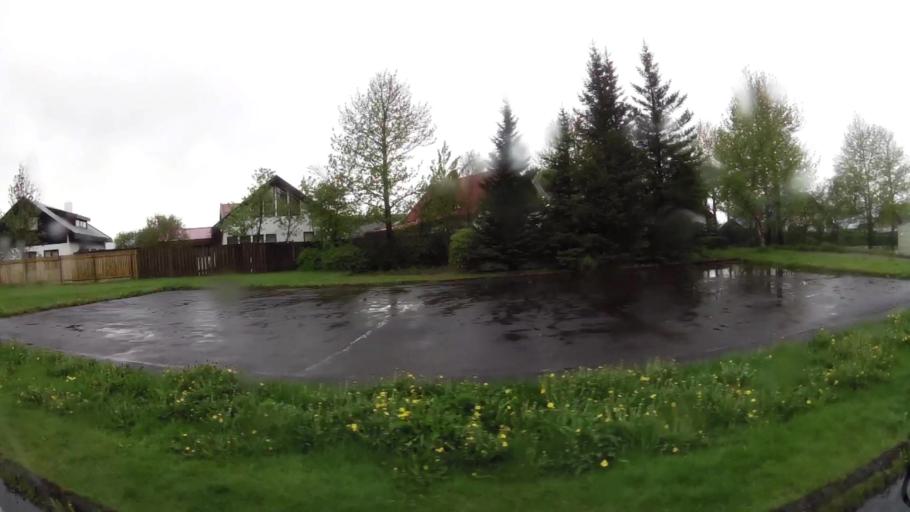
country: IS
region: Capital Region
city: Reykjavik
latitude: 64.0974
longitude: -21.8378
